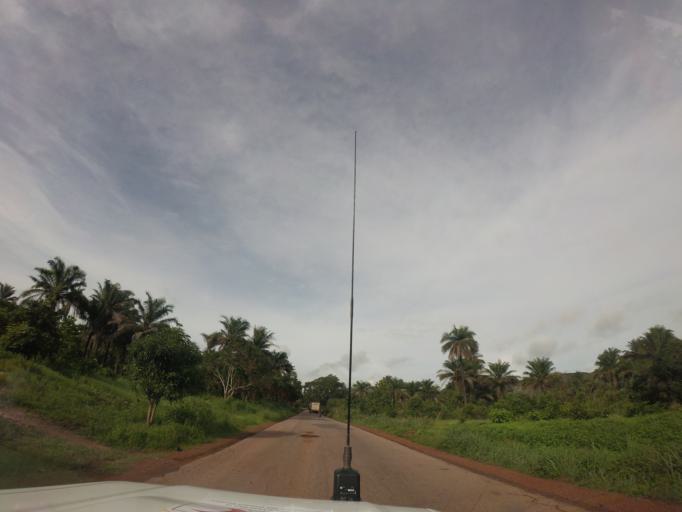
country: GN
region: Kindia
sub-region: Kindia
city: Kindia
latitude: 9.8907
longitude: -13.0541
